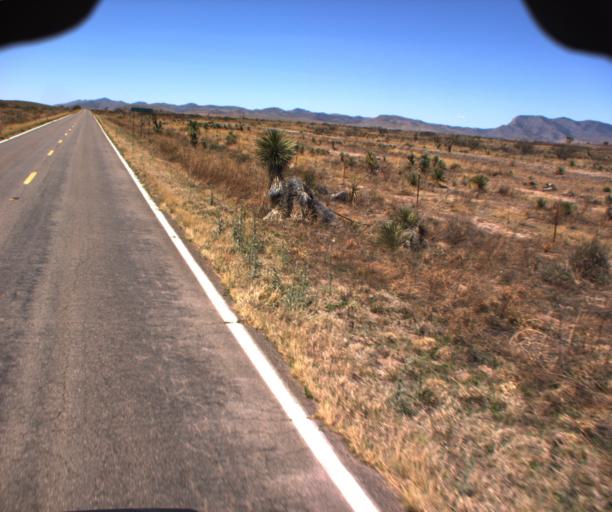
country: US
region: Arizona
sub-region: Cochise County
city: Douglas
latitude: 31.6336
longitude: -109.1929
